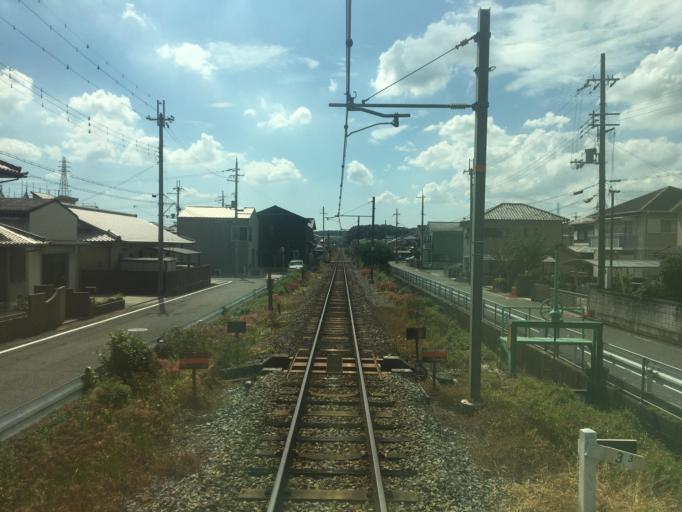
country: JP
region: Hyogo
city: Yashiro
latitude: 34.9393
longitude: 134.9523
